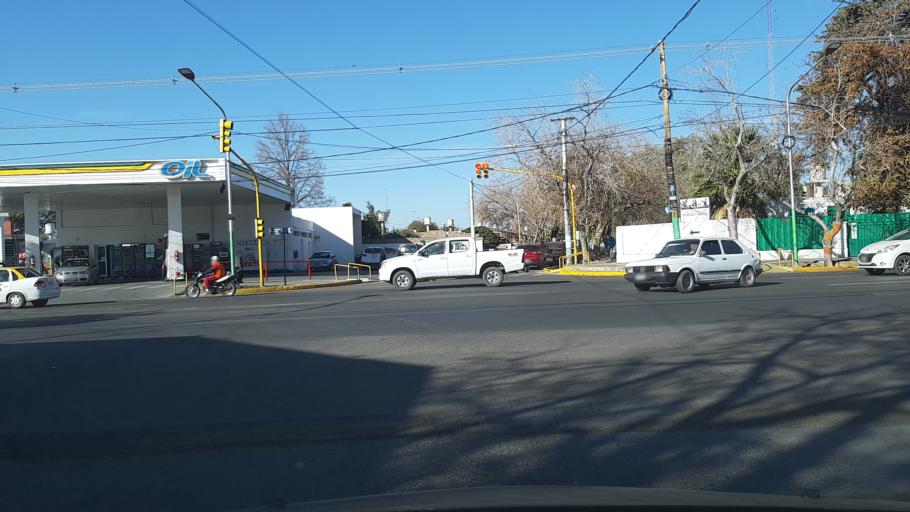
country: AR
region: San Juan
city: San Juan
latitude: -31.5298
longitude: -68.5914
